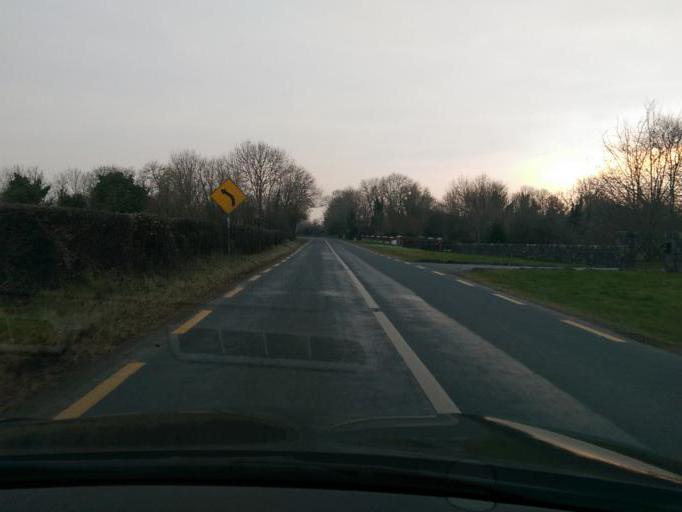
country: IE
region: Leinster
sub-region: An Longfort
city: Ballymahon
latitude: 53.5400
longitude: -7.7903
